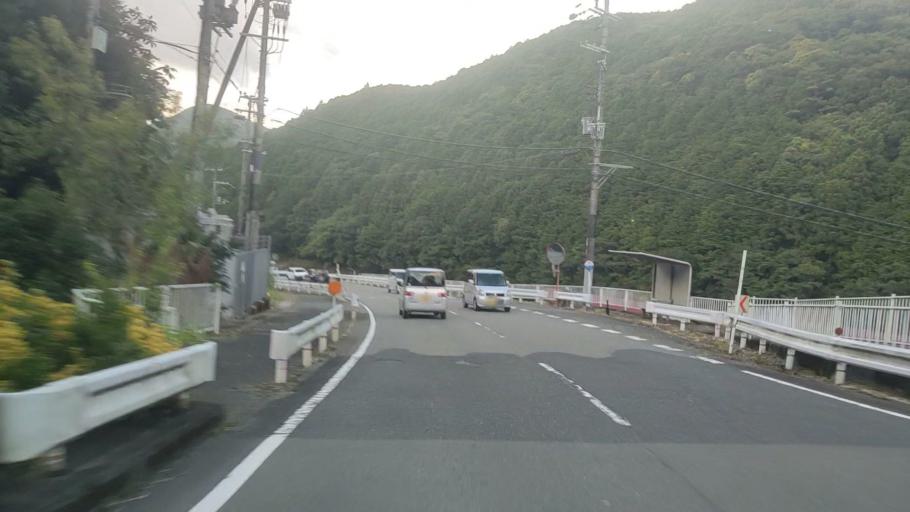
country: JP
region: Wakayama
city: Tanabe
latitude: 33.7822
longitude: 135.5058
